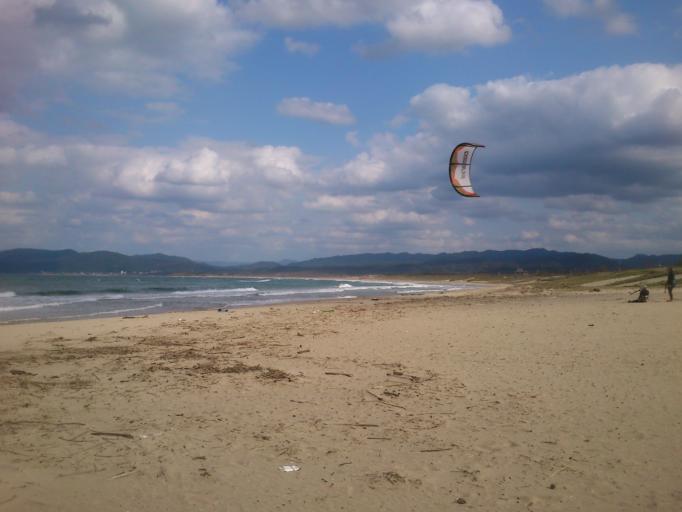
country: JP
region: Hyogo
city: Toyooka
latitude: 35.6456
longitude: 134.9036
